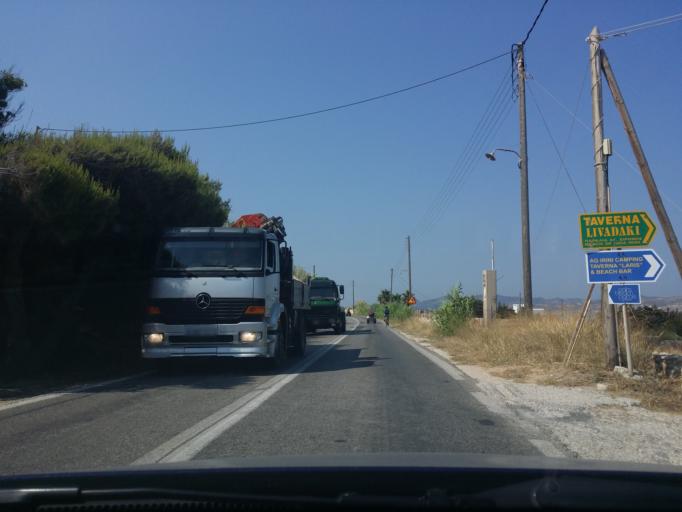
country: GR
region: South Aegean
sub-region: Nomos Kykladon
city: Paros
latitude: 37.0592
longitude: 25.1180
